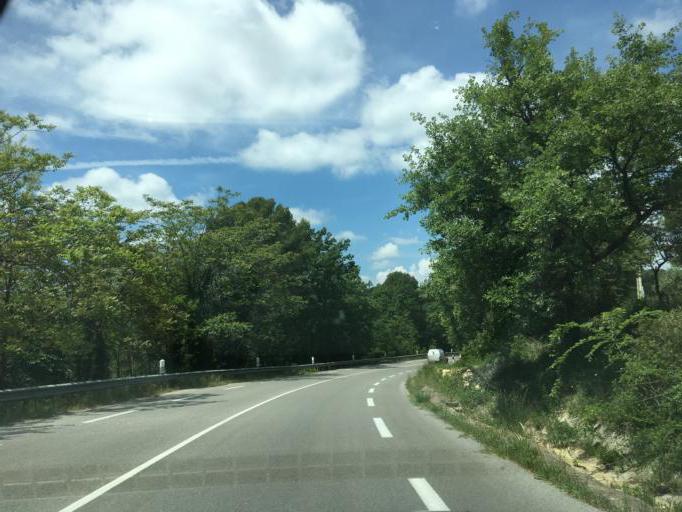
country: FR
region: Provence-Alpes-Cote d'Azur
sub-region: Departement du Var
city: Flayosc
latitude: 43.5415
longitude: 6.3628
